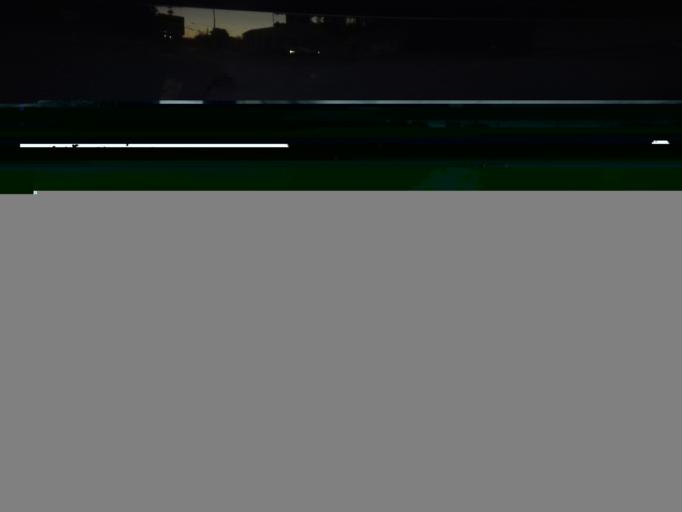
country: IE
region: Leinster
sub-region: Lu
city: Drogheda
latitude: 53.7198
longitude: -6.3758
